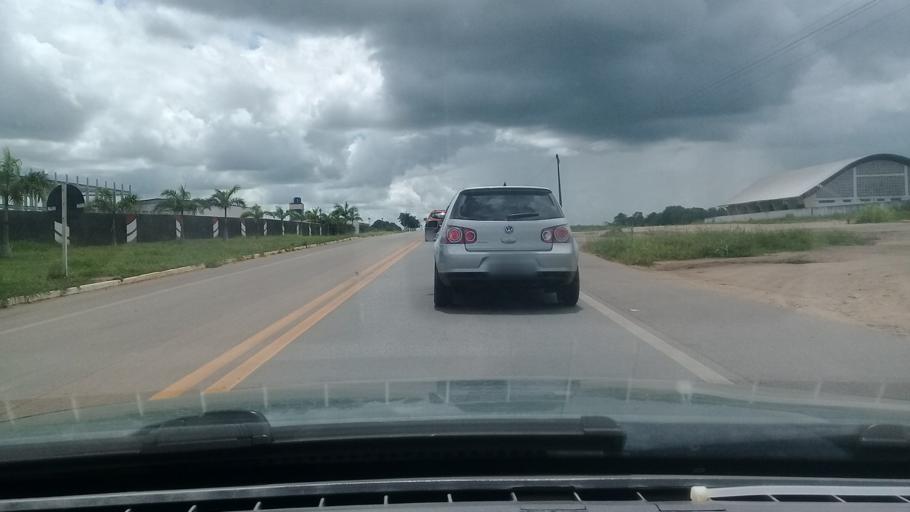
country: BR
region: Pernambuco
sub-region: Nazare Da Mata
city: Nazare da Mata
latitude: -7.7761
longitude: -35.2375
